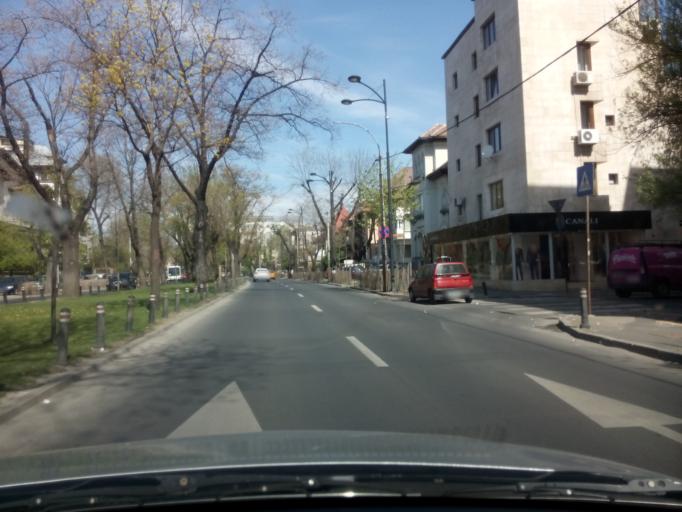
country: RO
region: Bucuresti
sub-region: Municipiul Bucuresti
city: Bucharest
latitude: 44.4616
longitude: 26.0934
